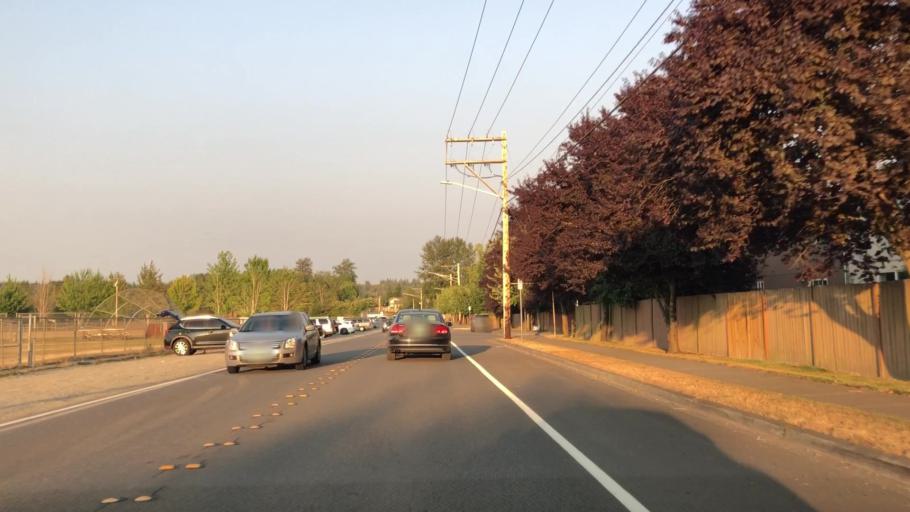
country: US
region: Washington
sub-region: Snohomish County
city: Marysville
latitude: 48.0921
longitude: -122.1539
